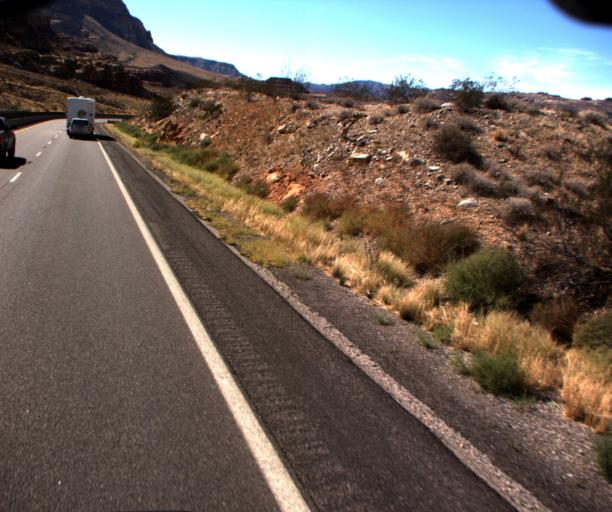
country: US
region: Utah
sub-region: Washington County
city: Santa Clara
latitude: 36.9721
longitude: -113.7151
